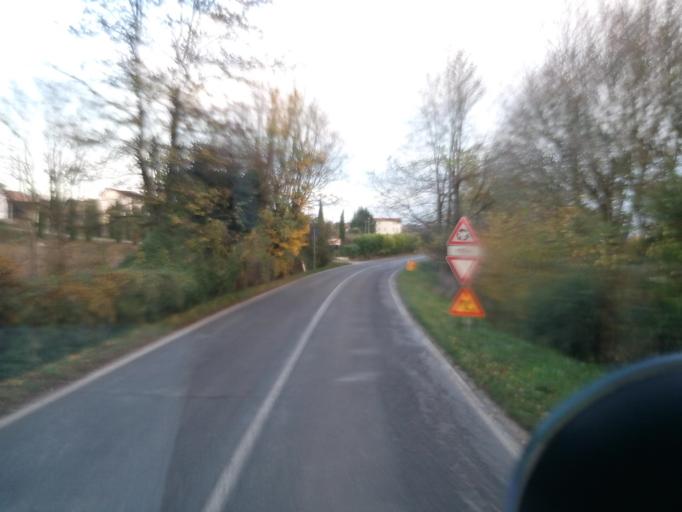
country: IT
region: Lombardy
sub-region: Provincia di Brescia
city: Pozzolengo
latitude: 45.4102
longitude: 10.6386
